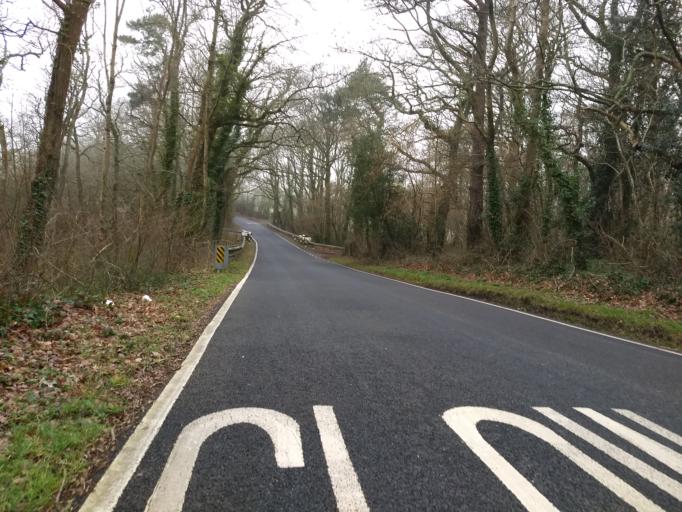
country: GB
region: England
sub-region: Isle of Wight
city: Newport
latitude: 50.7052
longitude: -1.2507
